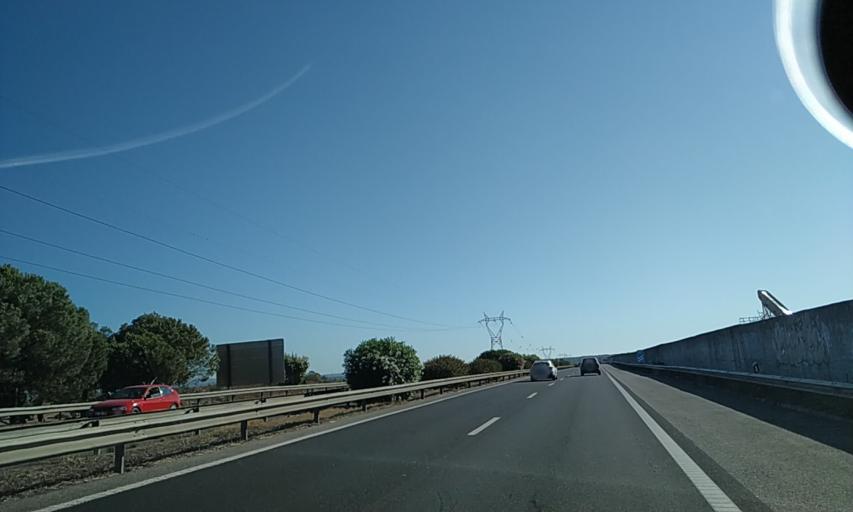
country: PT
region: Setubal
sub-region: Moita
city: Moita
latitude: 38.6505
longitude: -8.9694
